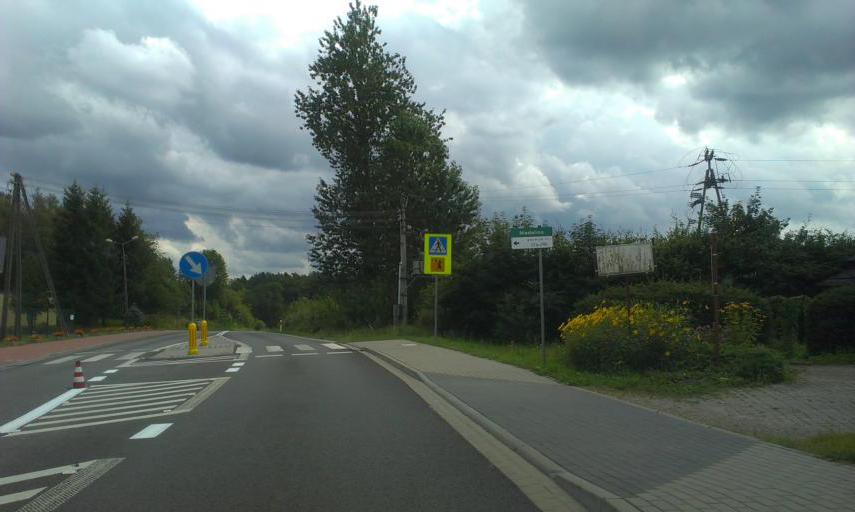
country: PL
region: West Pomeranian Voivodeship
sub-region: Koszalin
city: Koszalin
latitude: 54.0650
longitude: 16.1651
